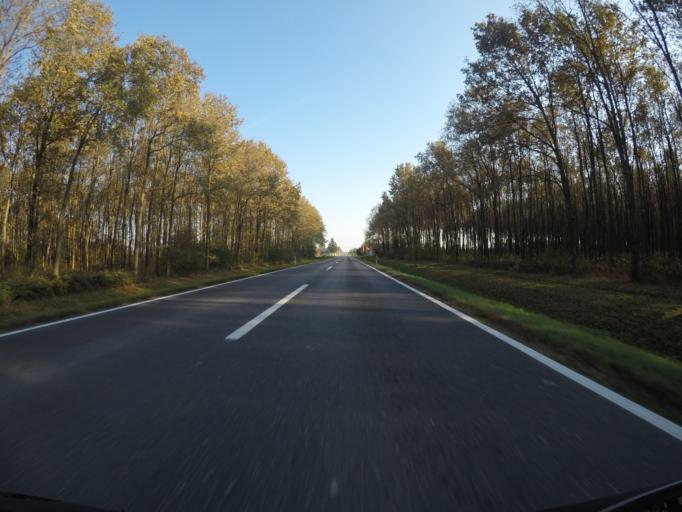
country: HR
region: Koprivnicko-Krizevacka
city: Kalinovac
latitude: 45.9929
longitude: 17.1278
